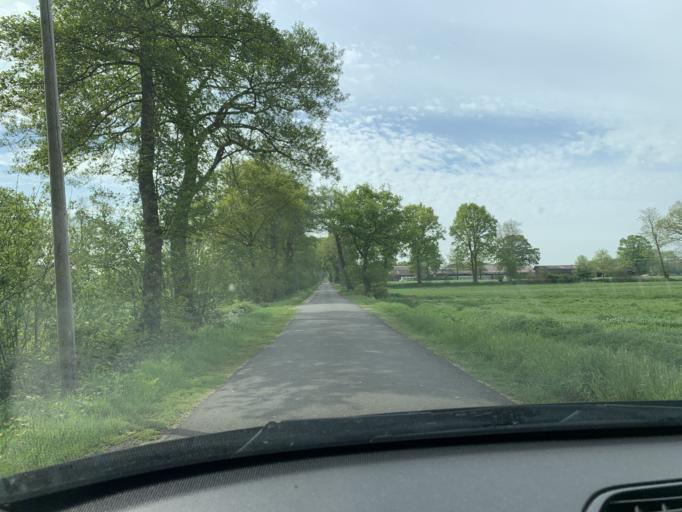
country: DE
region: Lower Saxony
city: Apen
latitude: 53.2343
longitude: 7.8126
